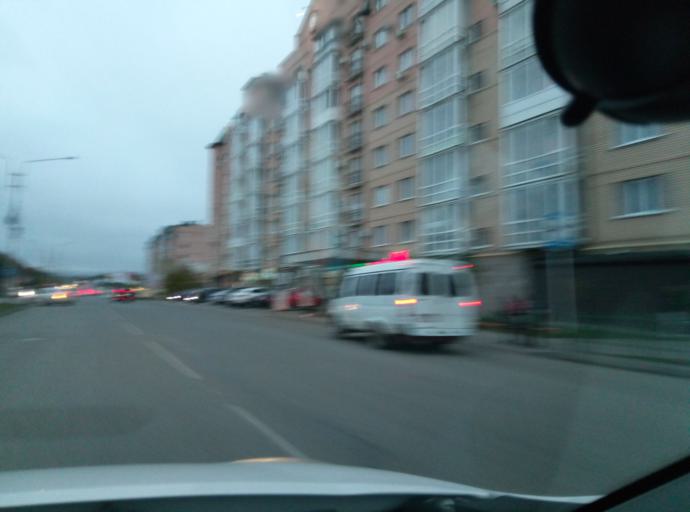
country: RU
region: Stavropol'skiy
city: Yessentukskaya
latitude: 44.0499
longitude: 42.8952
